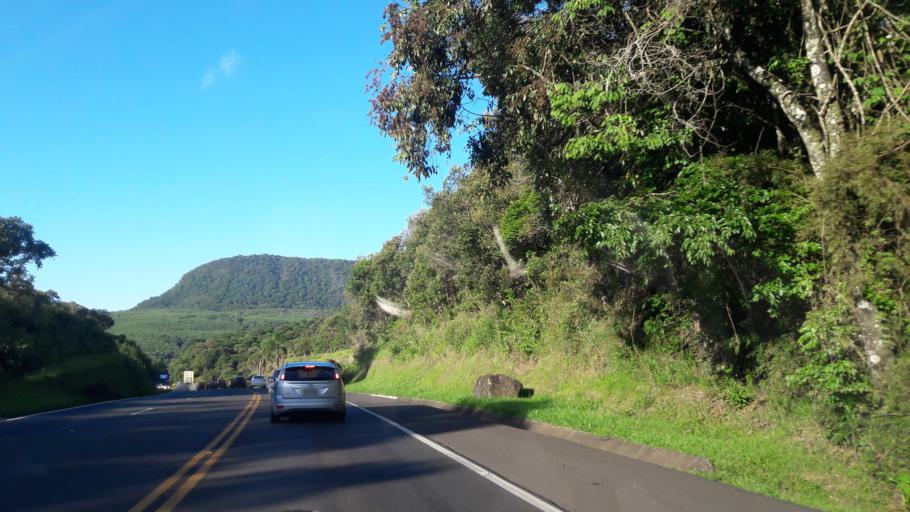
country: BR
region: Parana
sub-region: Prudentopolis
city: Prudentopolis
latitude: -25.3197
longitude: -51.1896
